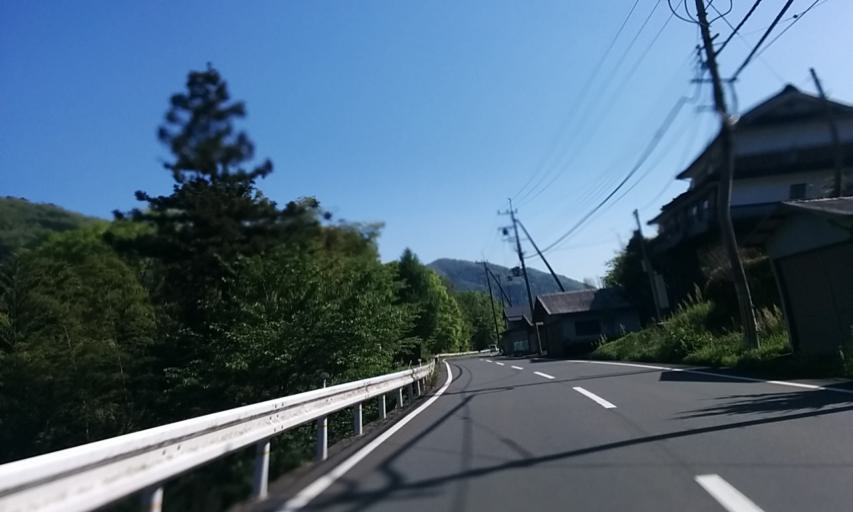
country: JP
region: Kyoto
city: Ayabe
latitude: 35.2619
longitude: 135.4292
